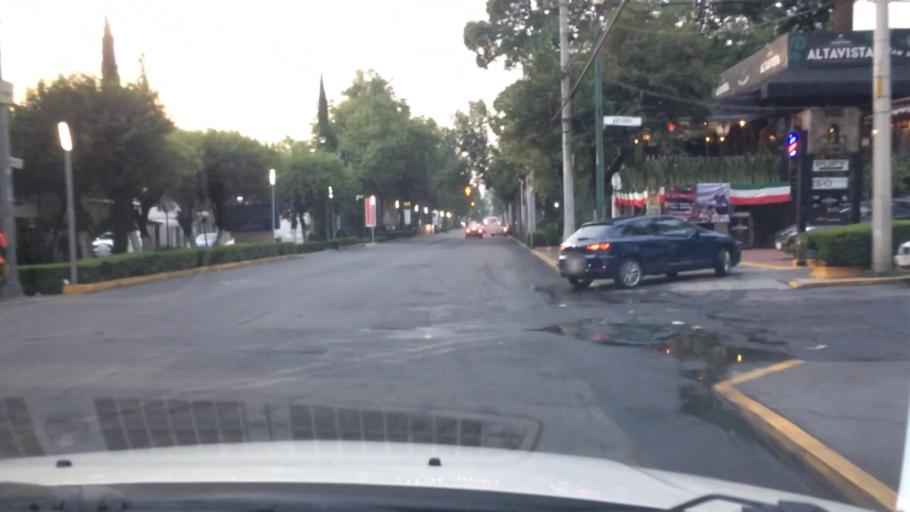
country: MX
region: Mexico City
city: Alvaro Obregon
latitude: 19.3491
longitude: -99.1962
